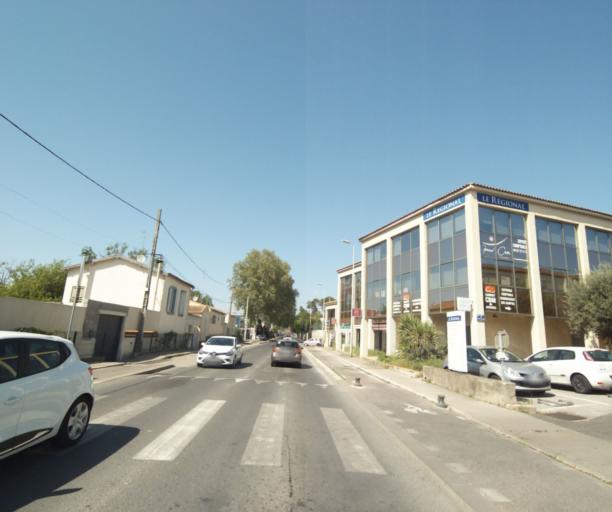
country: FR
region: Languedoc-Roussillon
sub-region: Departement de l'Herault
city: Castelnau-le-Lez
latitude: 43.6194
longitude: 3.8974
